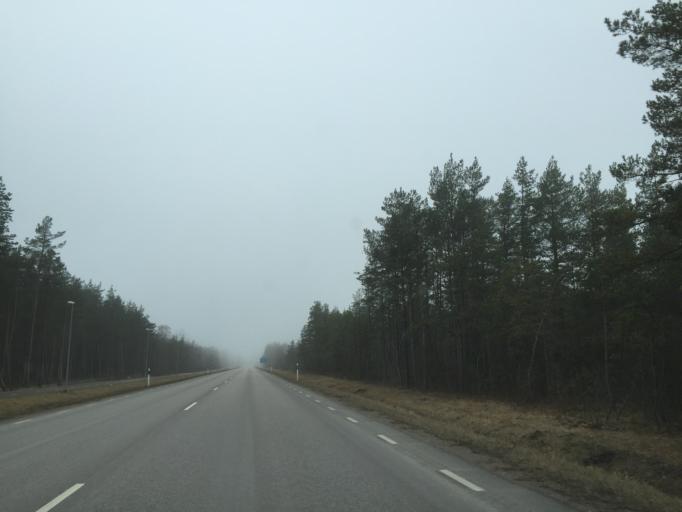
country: EE
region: Saare
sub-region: Kuressaare linn
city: Kuressaare
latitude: 58.2345
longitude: 22.4241
